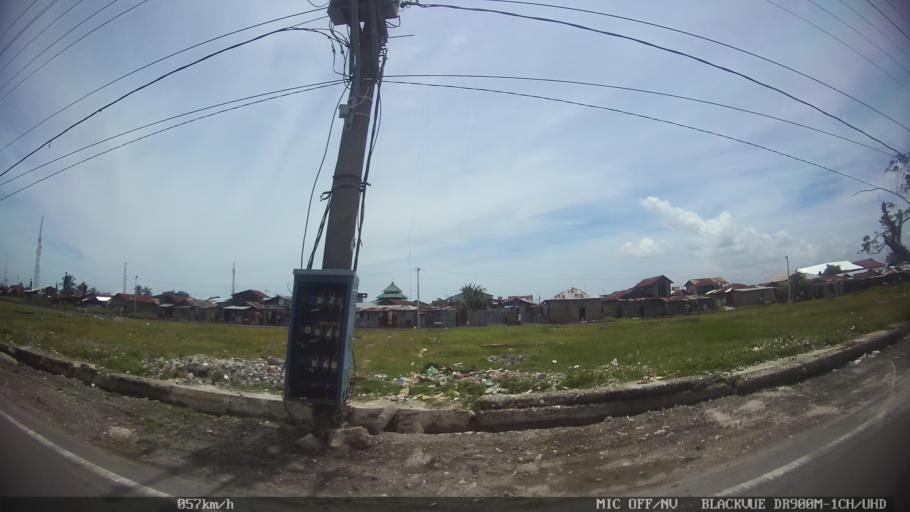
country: ID
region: North Sumatra
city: Belawan
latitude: 3.7773
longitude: 98.6813
